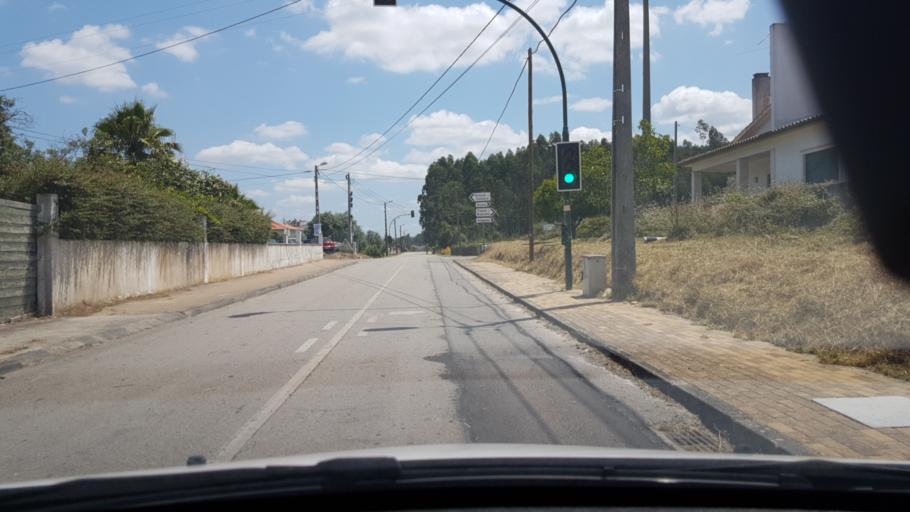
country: PT
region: Coimbra
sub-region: Soure
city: Alfarelos
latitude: 40.1558
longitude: -8.6352
